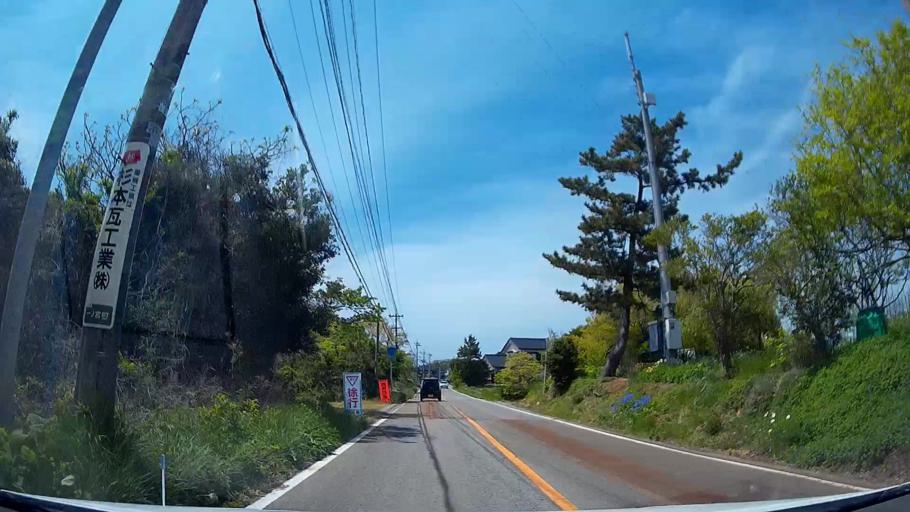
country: JP
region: Ishikawa
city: Hakui
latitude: 36.9251
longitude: 136.7627
